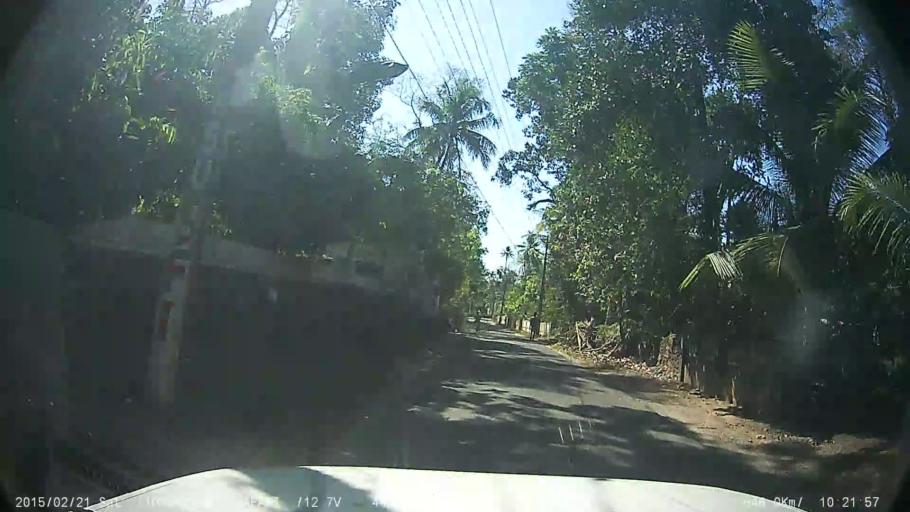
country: IN
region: Kerala
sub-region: Kottayam
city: Palackattumala
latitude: 9.8662
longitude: 76.6687
